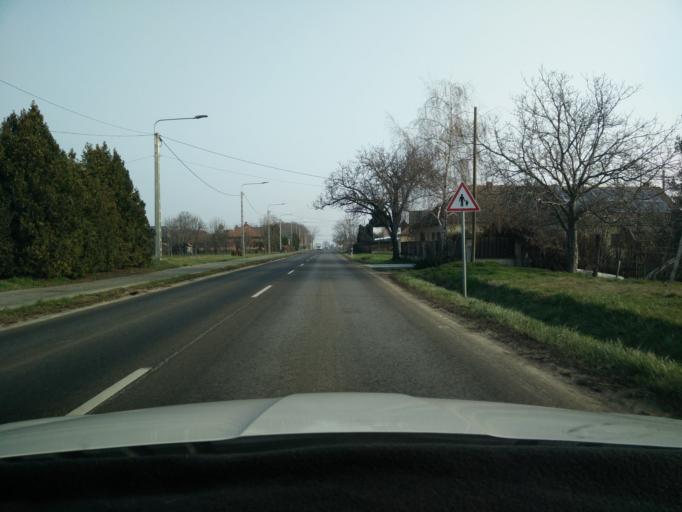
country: HU
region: Tolna
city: Szekszard
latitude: 46.3165
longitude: 18.6962
